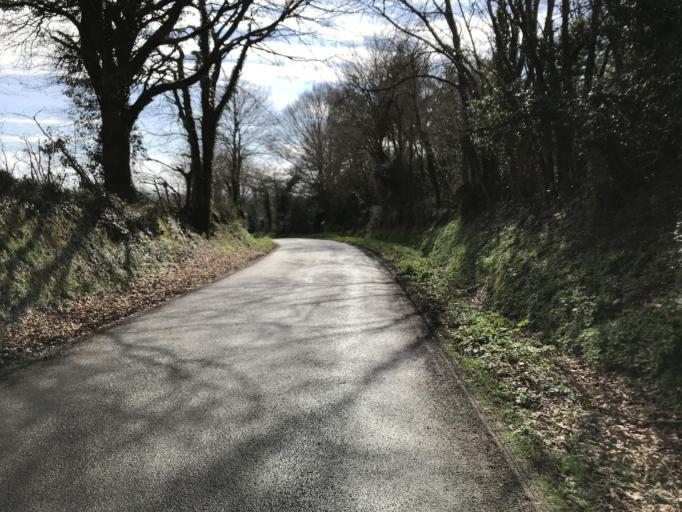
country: FR
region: Brittany
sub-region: Departement du Finistere
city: Daoulas
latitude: 48.3717
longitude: -4.2699
